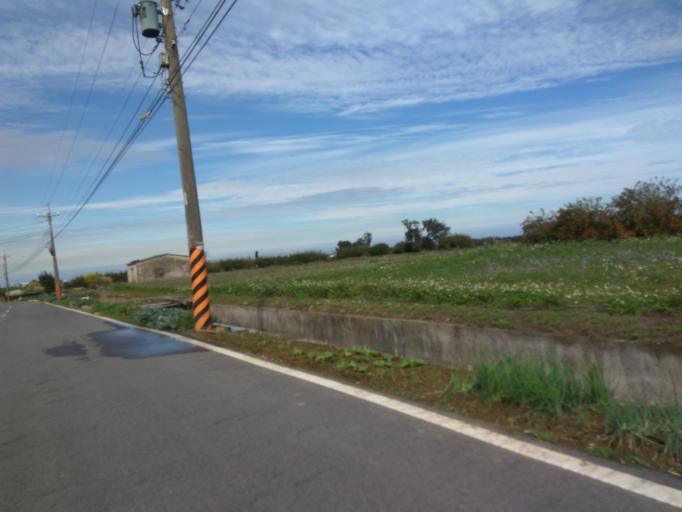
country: TW
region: Taiwan
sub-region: Hsinchu
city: Zhubei
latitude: 25.0033
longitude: 121.0844
